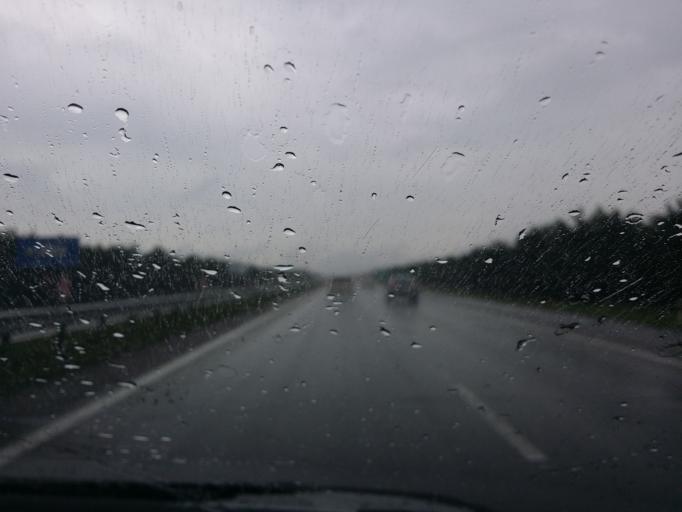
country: RU
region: Altai Krai
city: Zaton
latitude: 53.3194
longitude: 83.8814
